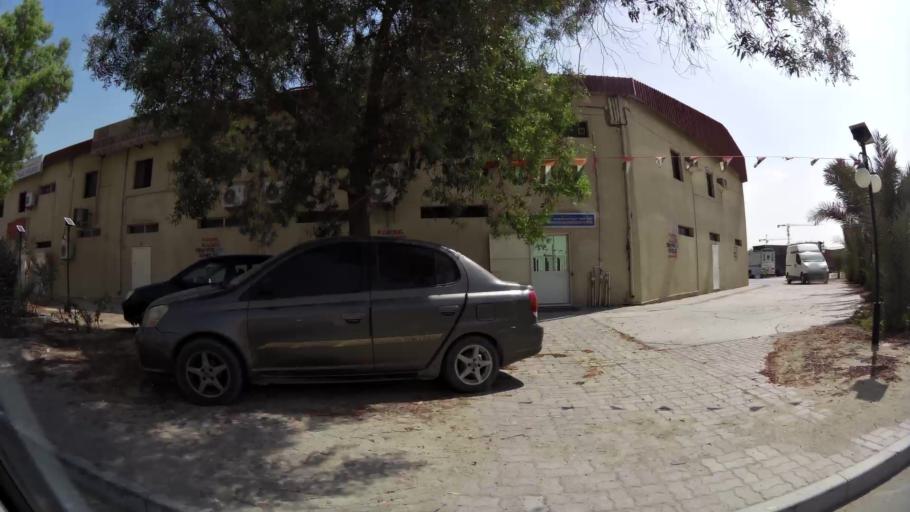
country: AE
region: Ash Shariqah
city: Sharjah
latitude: 25.2764
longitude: 55.3901
